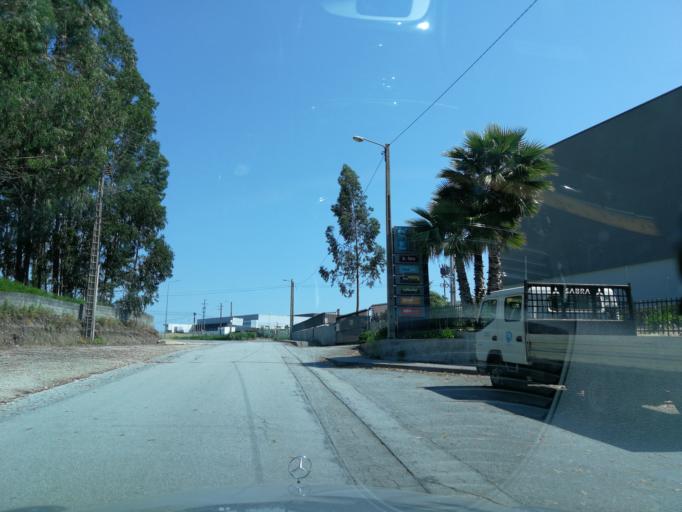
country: PT
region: Braga
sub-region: Braga
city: Adaufe
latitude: 41.5586
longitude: -8.3496
